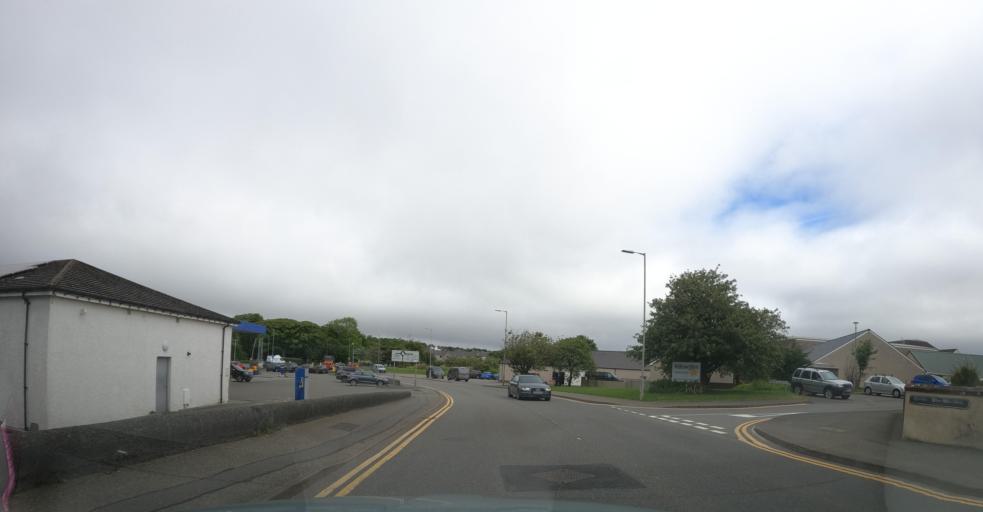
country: GB
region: Scotland
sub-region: Eilean Siar
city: Isle of Lewis
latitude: 58.2156
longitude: -6.3844
